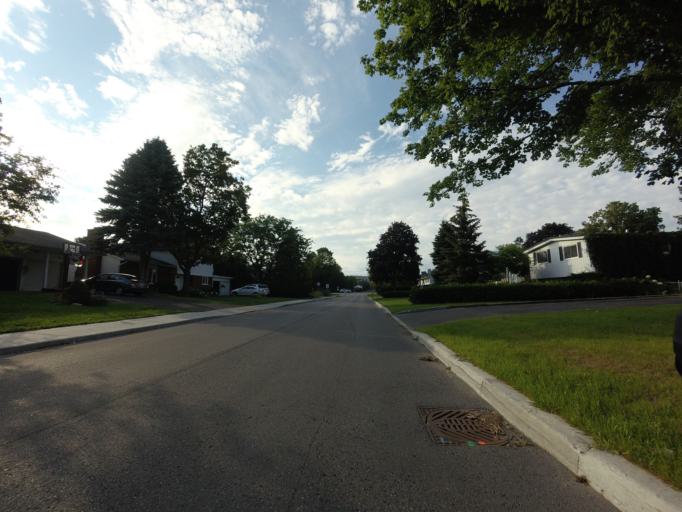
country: CA
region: Ontario
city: Bells Corners
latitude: 45.2828
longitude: -75.7663
